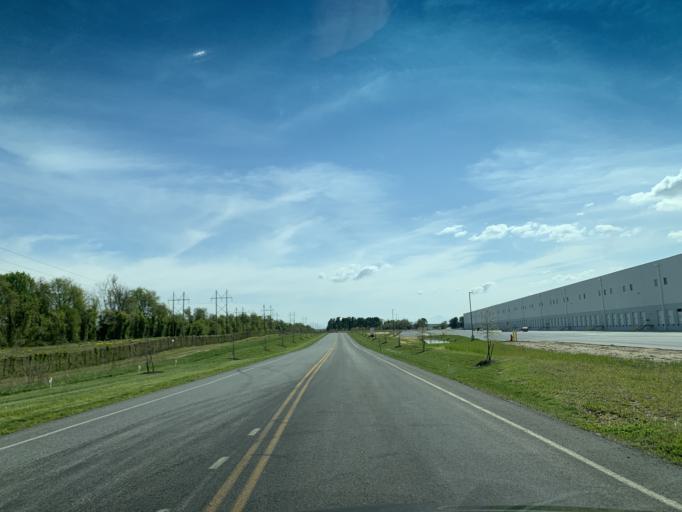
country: US
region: Maryland
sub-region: Harford County
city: Perryman
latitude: 39.4712
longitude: -76.1911
